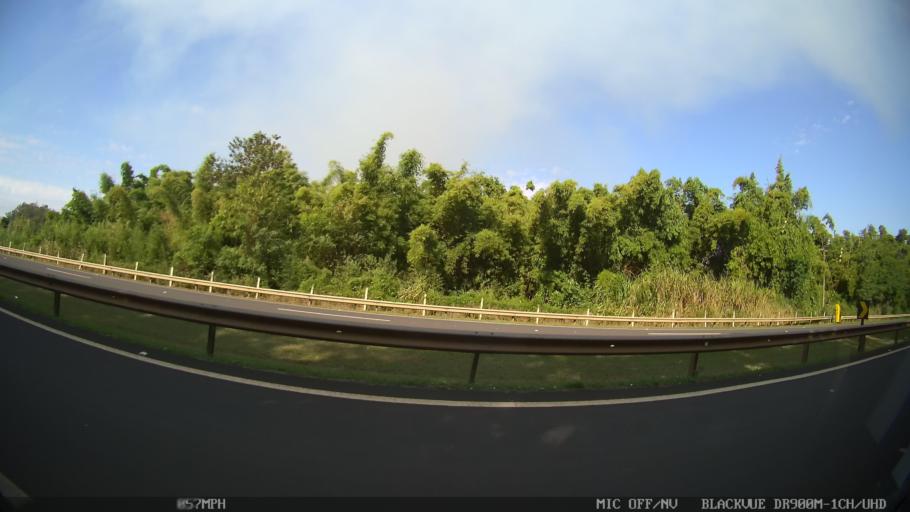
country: BR
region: Sao Paulo
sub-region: Piracicaba
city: Piracicaba
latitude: -22.6955
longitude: -47.5915
